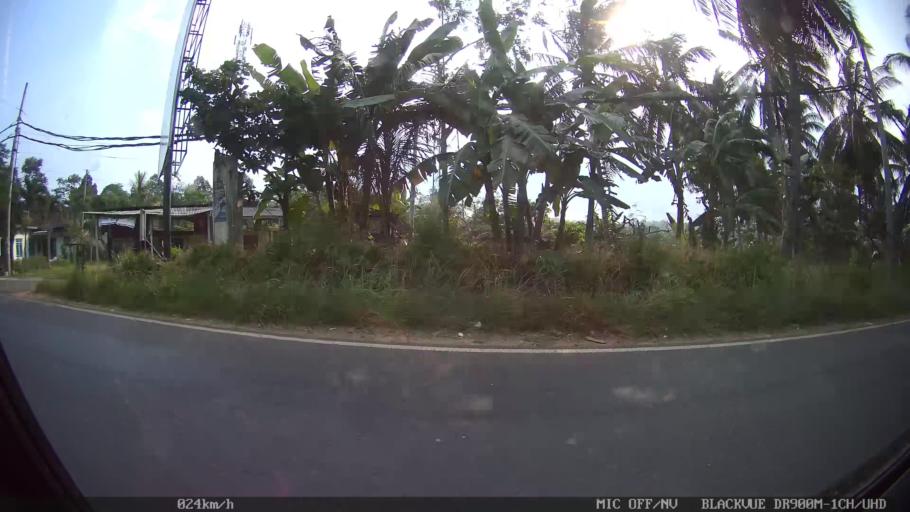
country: ID
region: Lampung
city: Natar
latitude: -5.3664
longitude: 105.1882
